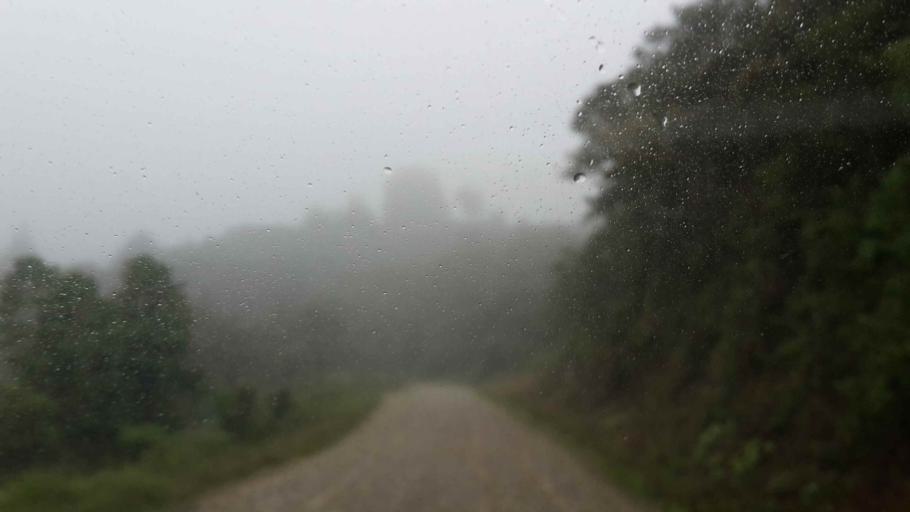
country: BO
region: Cochabamba
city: Colomi
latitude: -17.1653
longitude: -65.8966
